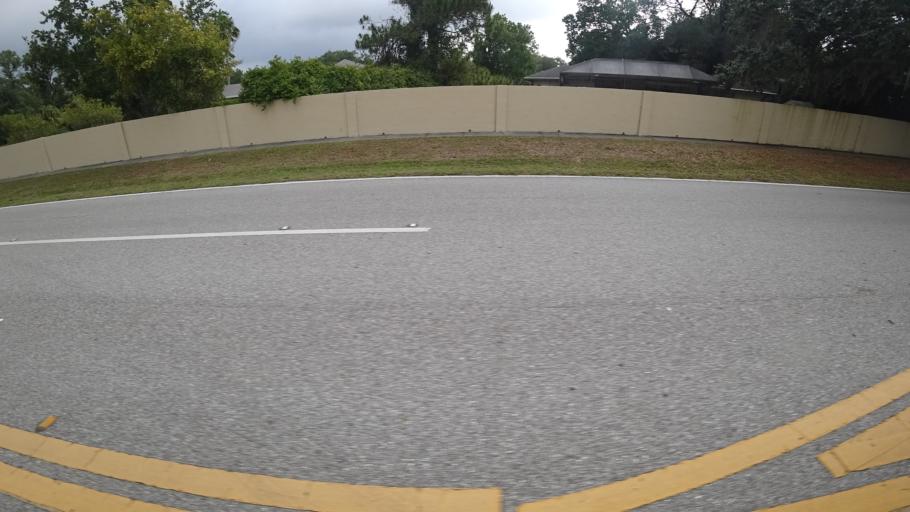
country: US
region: Florida
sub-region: Manatee County
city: Samoset
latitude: 27.4541
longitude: -82.5260
